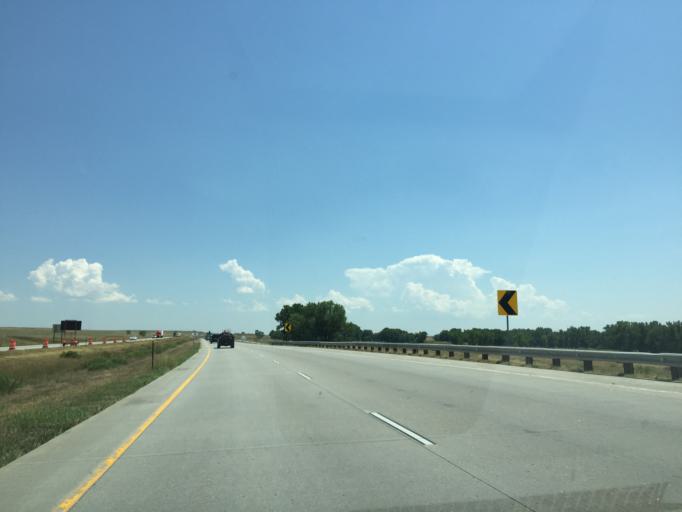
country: US
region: Colorado
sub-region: Arapahoe County
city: Byers
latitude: 39.4984
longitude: -103.9668
